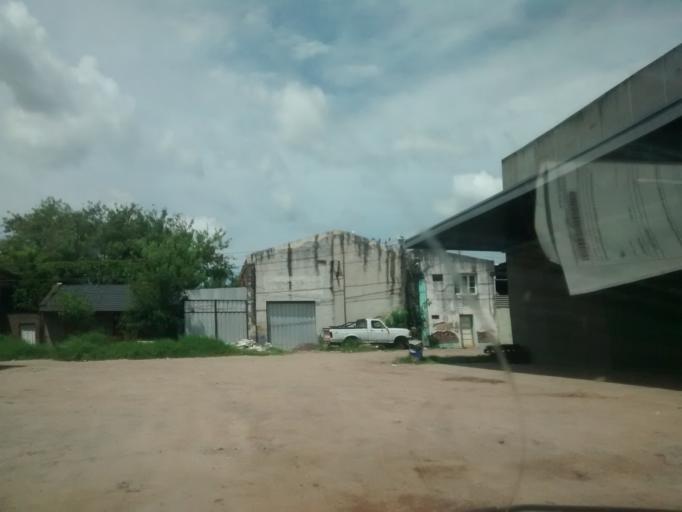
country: AR
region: Chaco
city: Resistencia
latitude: -27.4474
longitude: -58.9983
